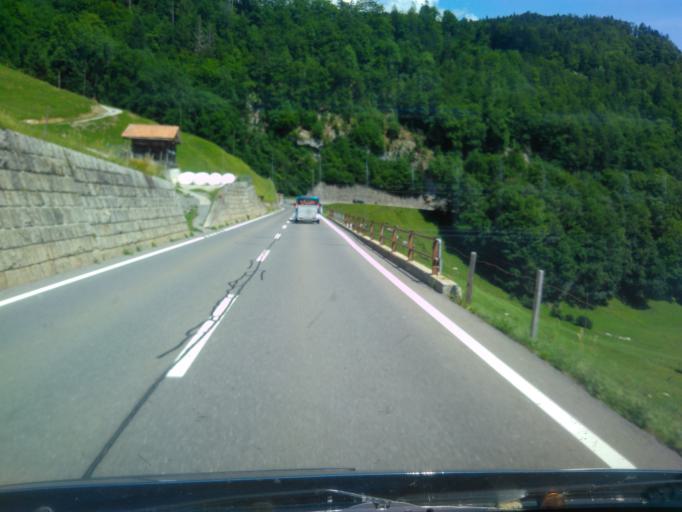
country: CH
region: Obwalden
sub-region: Obwalden
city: Lungern
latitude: 46.7542
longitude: 8.1330
